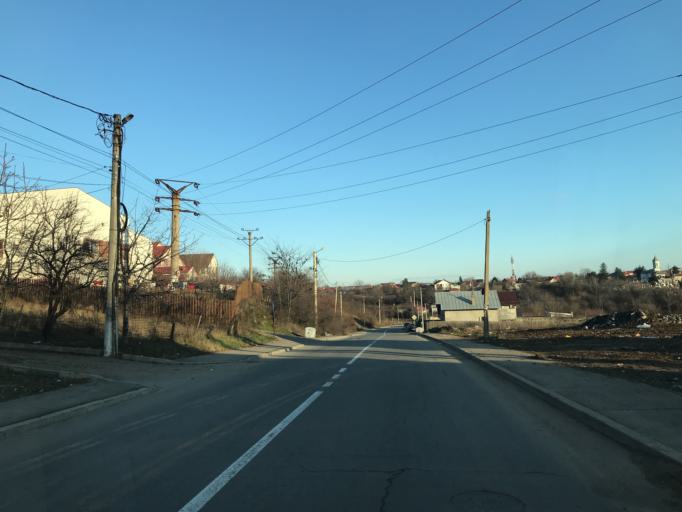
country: RO
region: Olt
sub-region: Municipiul Slatina
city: Slatina
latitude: 44.4179
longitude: 24.3650
